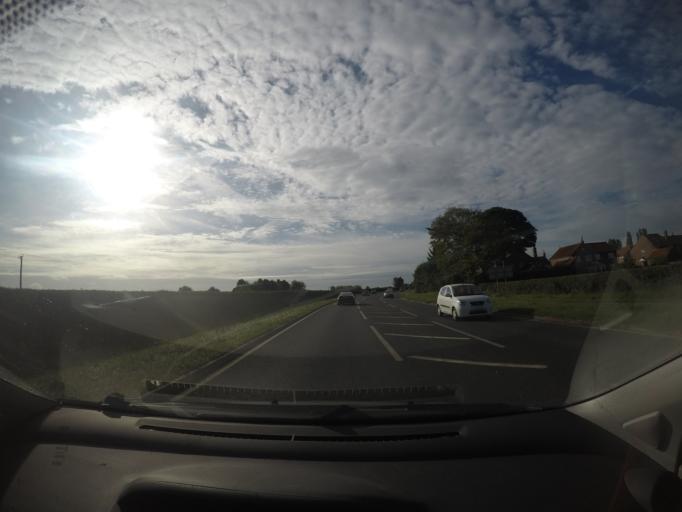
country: GB
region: England
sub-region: City of York
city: Deighton
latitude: 53.8912
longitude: -1.0455
